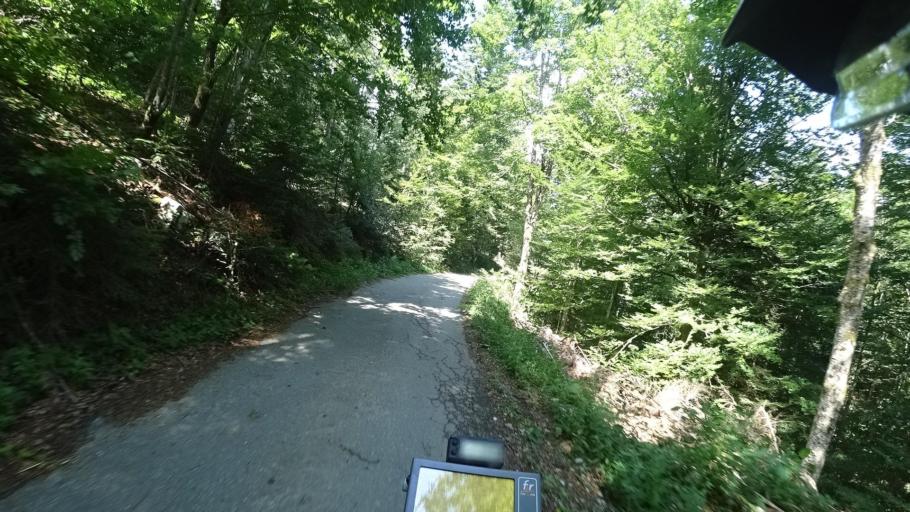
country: HR
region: Licko-Senjska
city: Brinje
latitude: 45.1205
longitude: 15.0385
